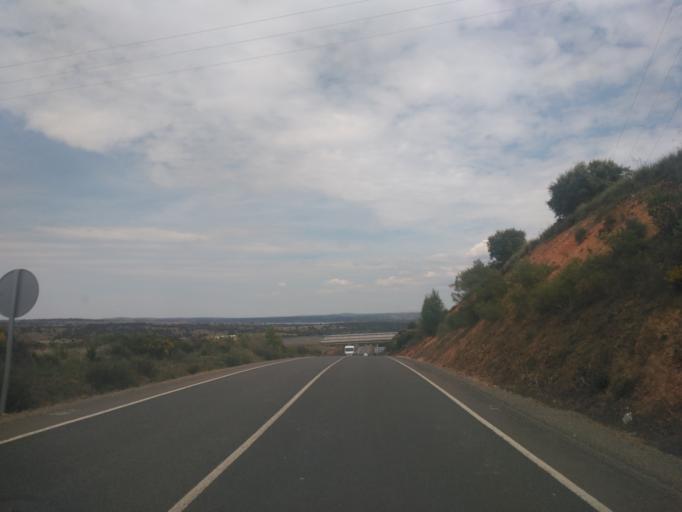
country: ES
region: Castille and Leon
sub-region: Provincia de Salamanca
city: Guijuelo
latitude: 40.5550
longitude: -5.6607
